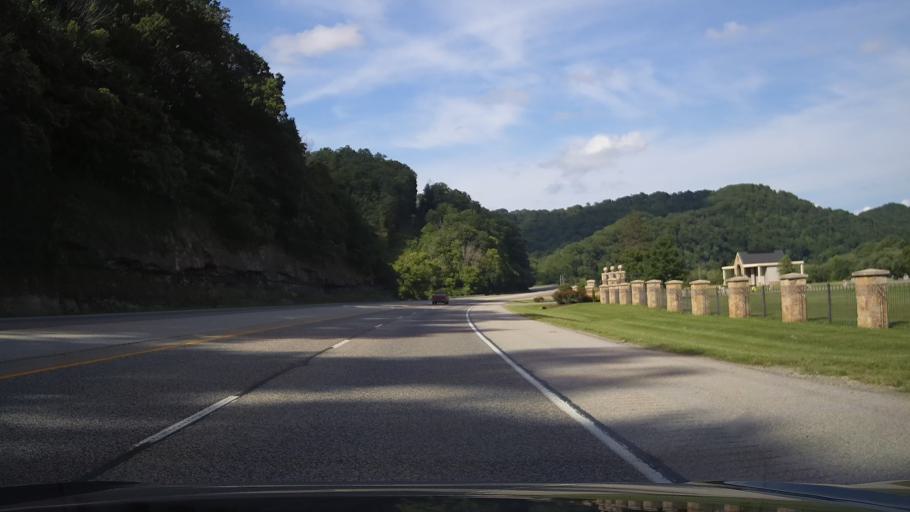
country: US
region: Kentucky
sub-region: Lawrence County
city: Louisa
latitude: 38.0174
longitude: -82.6570
